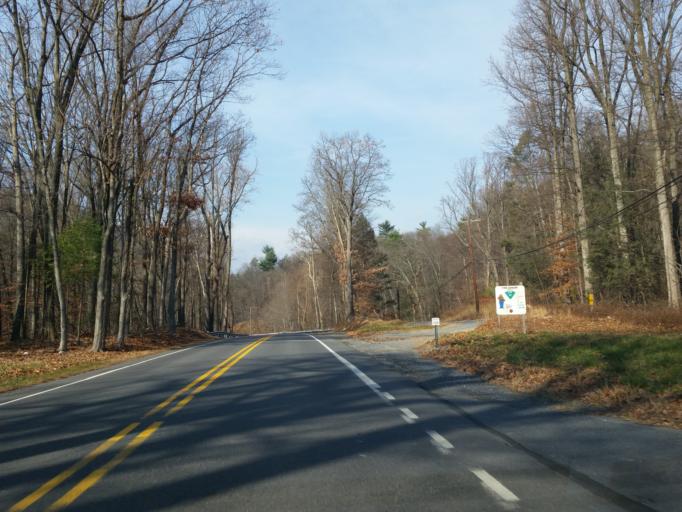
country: US
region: Pennsylvania
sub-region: Lebanon County
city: Jonestown
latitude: 40.4364
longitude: -76.5953
